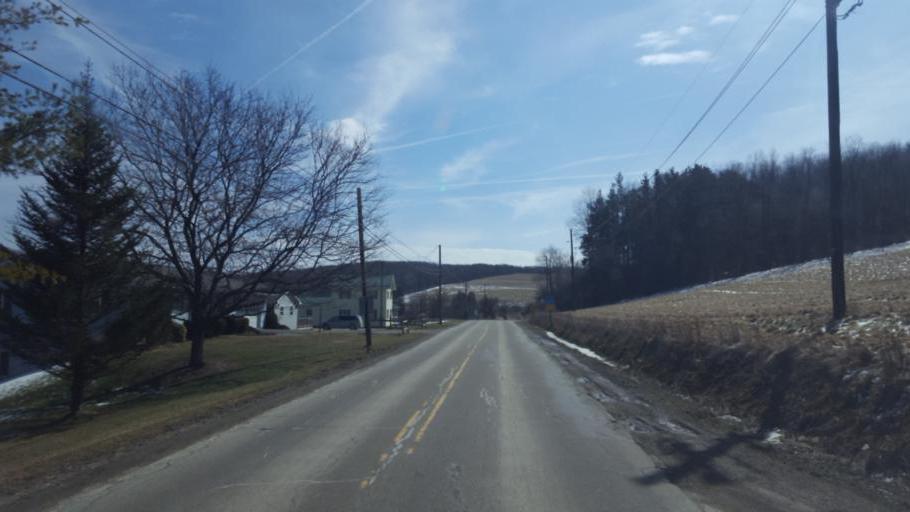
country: US
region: Pennsylvania
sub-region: Potter County
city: Galeton
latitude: 41.8974
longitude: -77.7611
